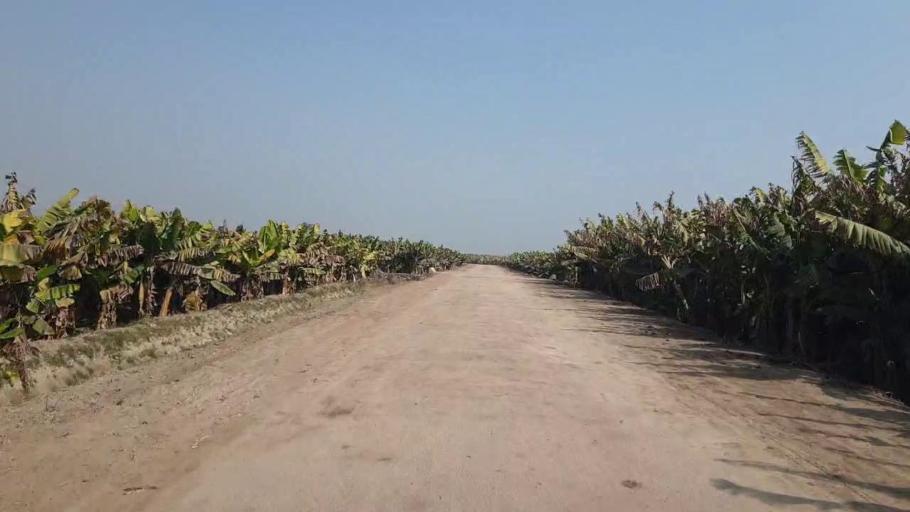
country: PK
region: Sindh
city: Bhit Shah
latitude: 25.7909
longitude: 68.4998
